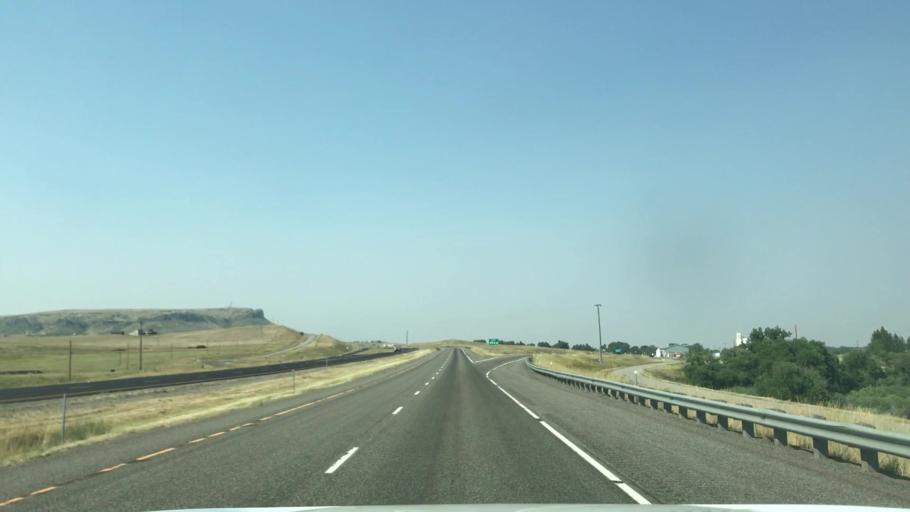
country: US
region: Montana
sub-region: Cascade County
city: Sun Prairie
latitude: 47.2562
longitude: -111.7091
